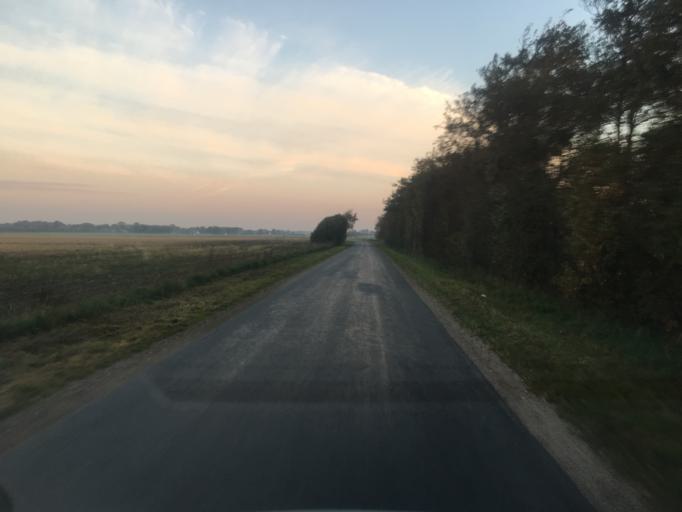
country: DK
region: South Denmark
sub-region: Tonder Kommune
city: Logumkloster
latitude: 54.9912
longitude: 9.0508
